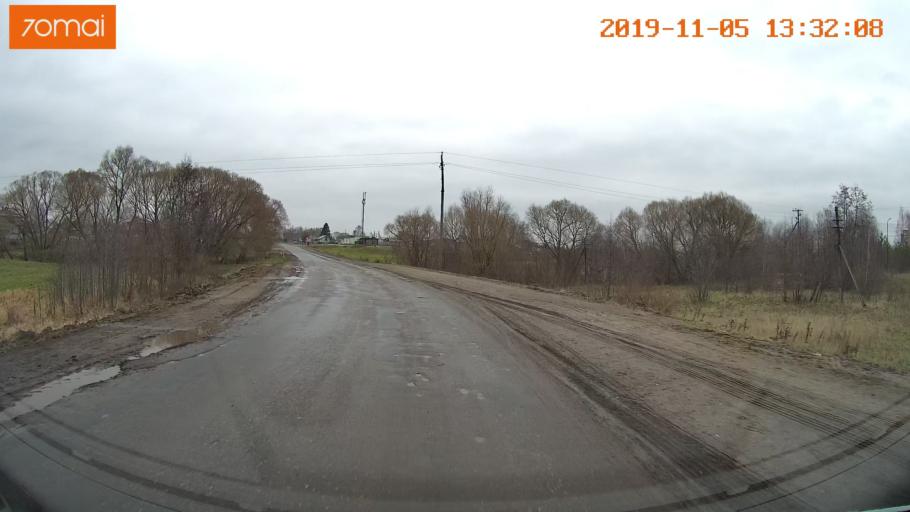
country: RU
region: Ivanovo
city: Shuya
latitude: 56.8810
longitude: 41.3983
